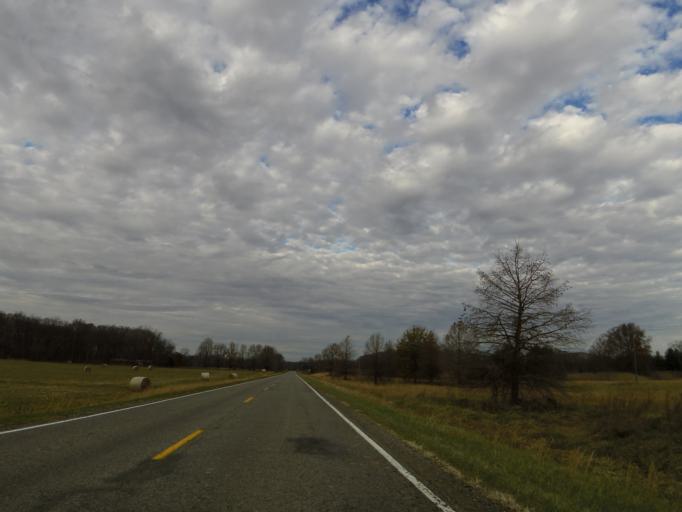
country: US
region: Illinois
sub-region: Jefferson County
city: Mount Vernon
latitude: 38.3665
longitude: -88.9864
